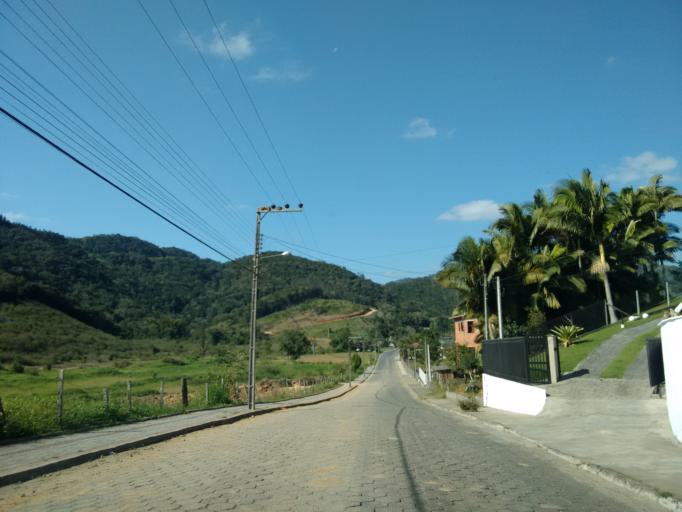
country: BR
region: Santa Catarina
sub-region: Pomerode
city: Pomerode
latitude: -26.7387
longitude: -49.1695
